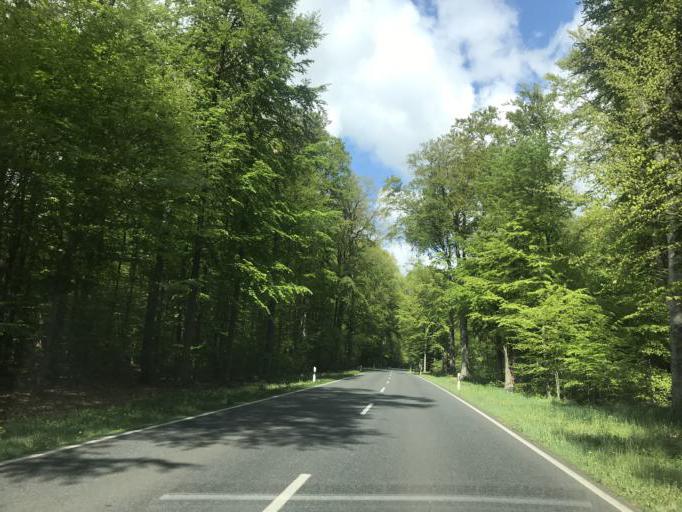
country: DE
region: Brandenburg
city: Marienwerder
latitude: 52.8621
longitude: 13.5226
